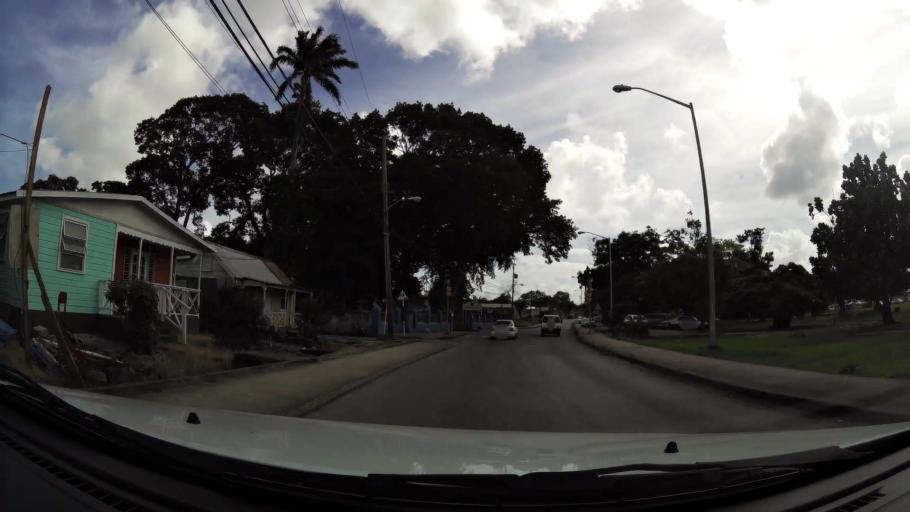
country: BB
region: Saint Michael
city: Bridgetown
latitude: 13.0978
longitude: -59.6057
